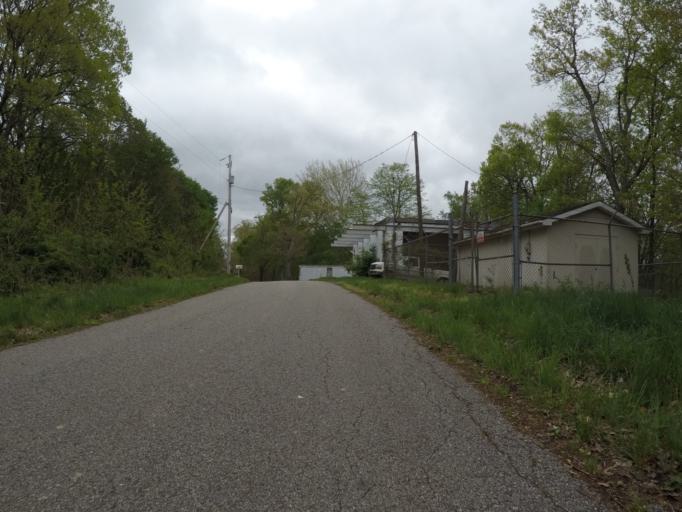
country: US
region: West Virginia
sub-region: Cabell County
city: Barboursville
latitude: 38.3997
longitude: -82.2623
